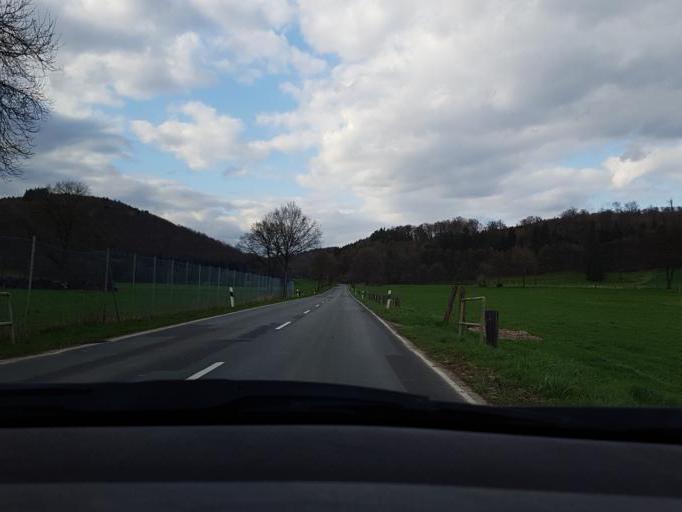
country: DE
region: Lower Saxony
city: Bodenfelde
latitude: 51.6522
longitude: 9.5483
